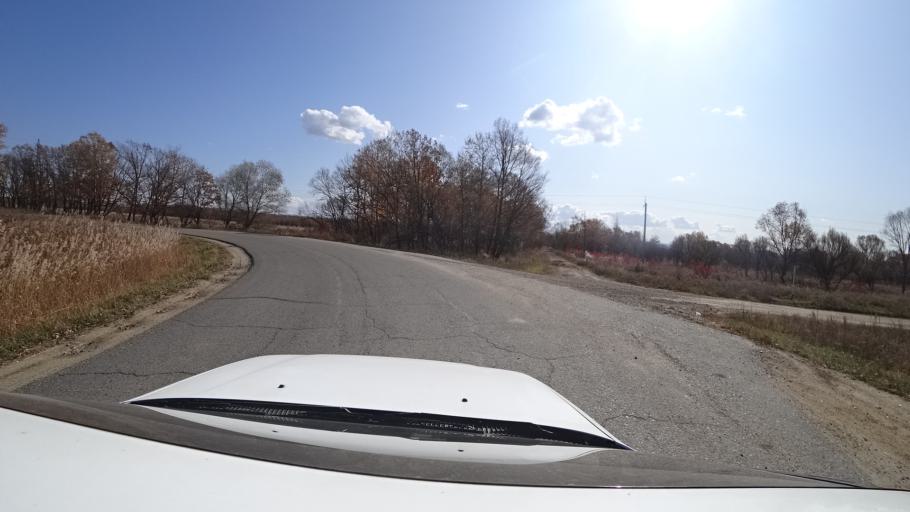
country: RU
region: Primorskiy
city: Lazo
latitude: 45.8682
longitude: 133.6620
